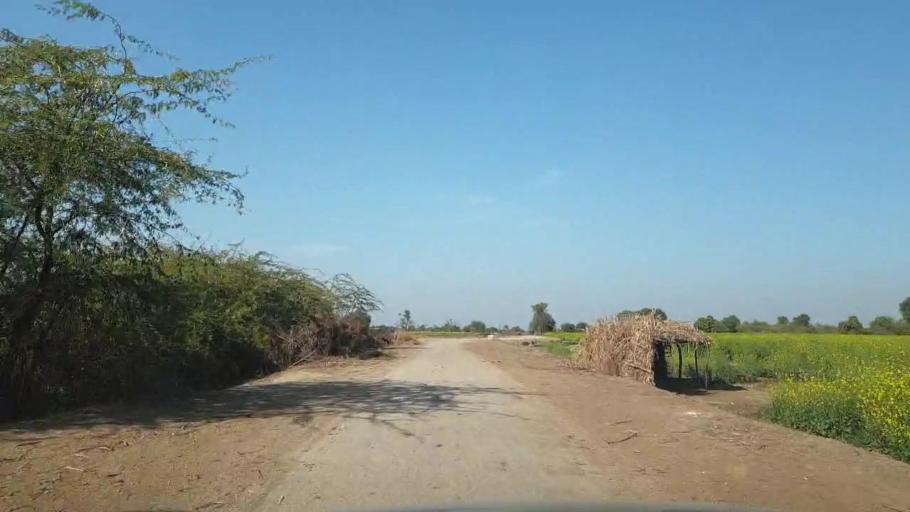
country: PK
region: Sindh
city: Tando Adam
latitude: 25.6737
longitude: 68.6861
